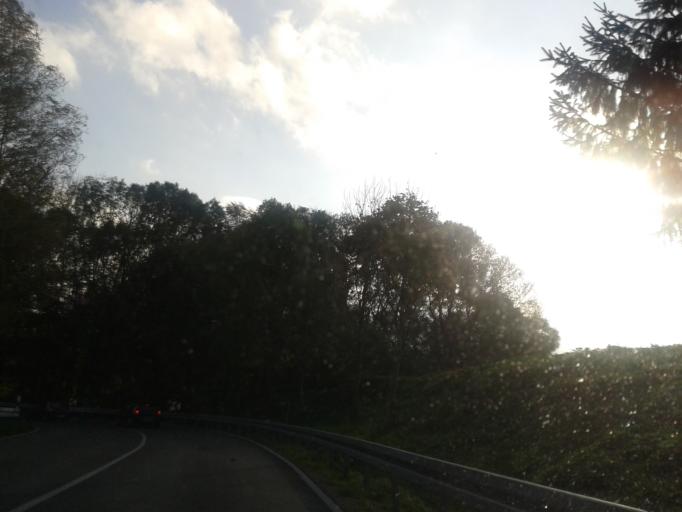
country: DE
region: Saxony
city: Nossen
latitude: 51.0238
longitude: 13.3249
